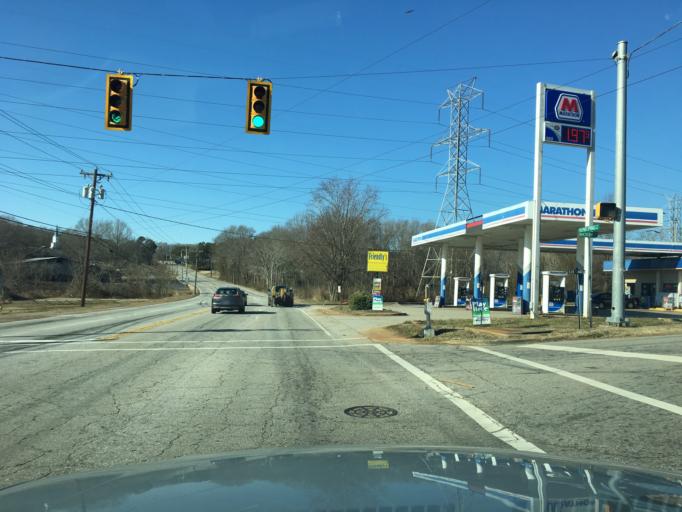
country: US
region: South Carolina
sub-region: Greenville County
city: Berea
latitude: 34.8936
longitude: -82.4447
